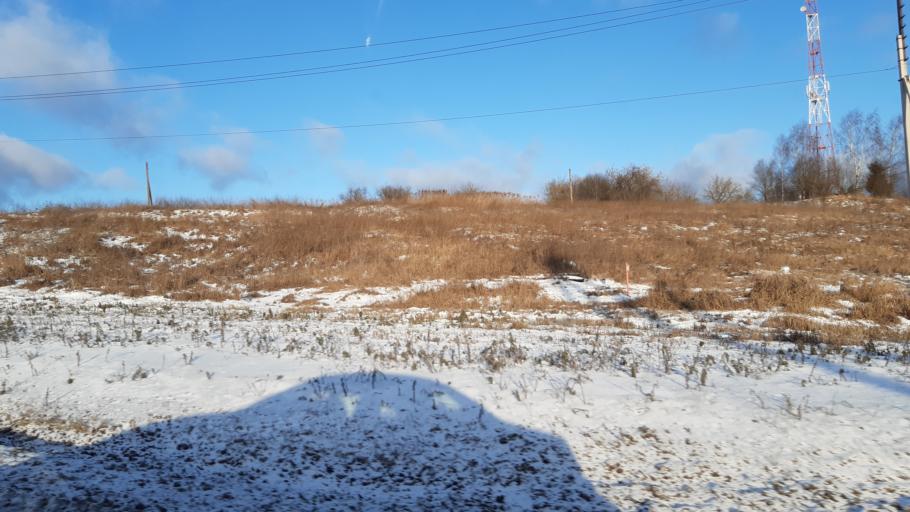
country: RU
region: Vladimir
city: Arsaki
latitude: 56.2846
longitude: 38.3947
